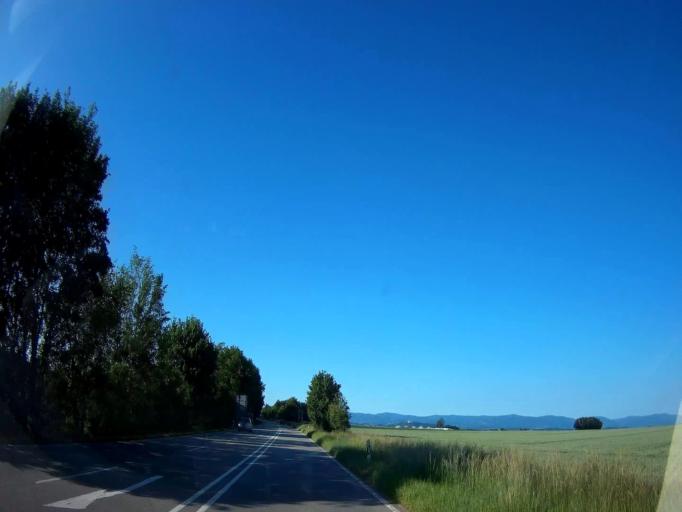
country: DE
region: Bavaria
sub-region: Lower Bavaria
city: Alterhofen
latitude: 48.8466
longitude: 12.6289
